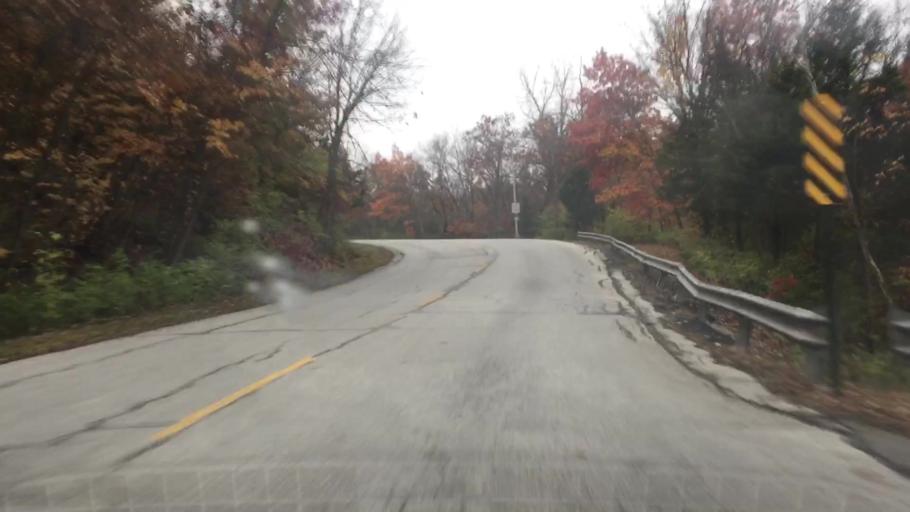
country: US
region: Missouri
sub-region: Callaway County
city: Fulton
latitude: 38.8432
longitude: -91.9543
